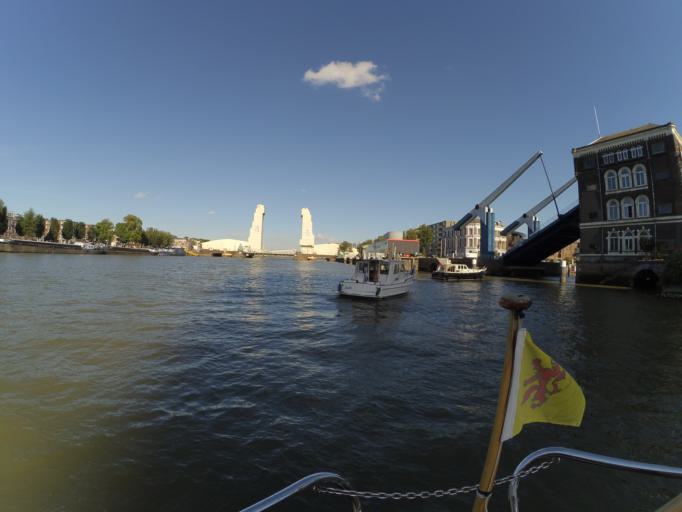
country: NL
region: South Holland
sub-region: Gemeente Rotterdam
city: Rotterdam
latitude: 51.9105
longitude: 4.4950
